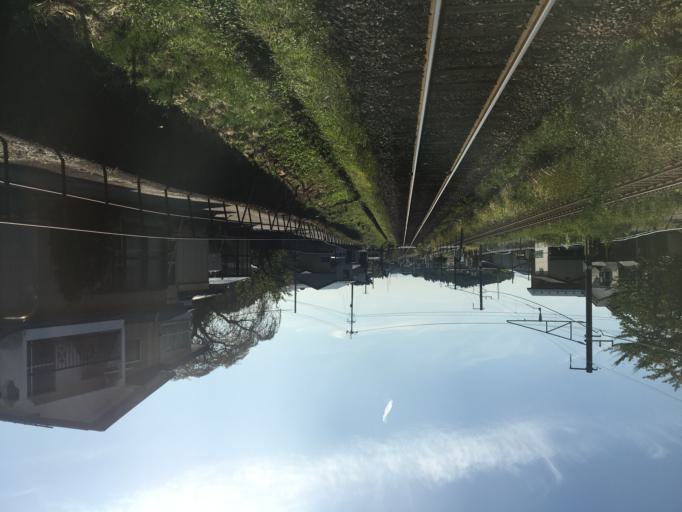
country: JP
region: Akita
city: Kakunodatemachi
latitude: 39.5962
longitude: 140.5738
